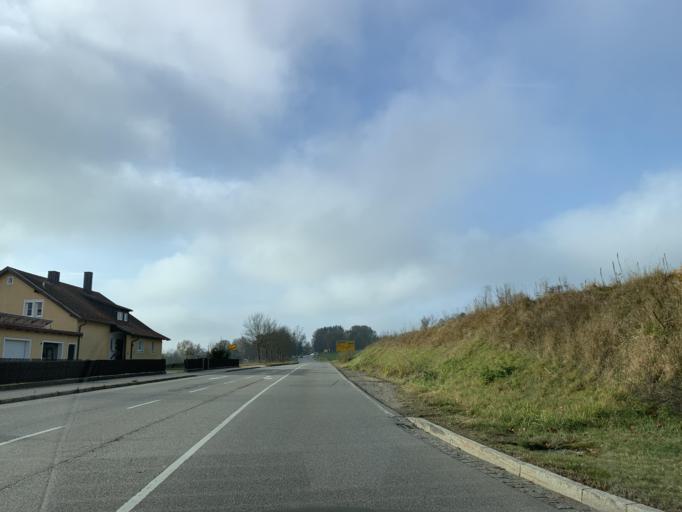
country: DE
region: Bavaria
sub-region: Upper Palatinate
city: Bodenwohr
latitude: 49.2665
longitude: 12.2987
